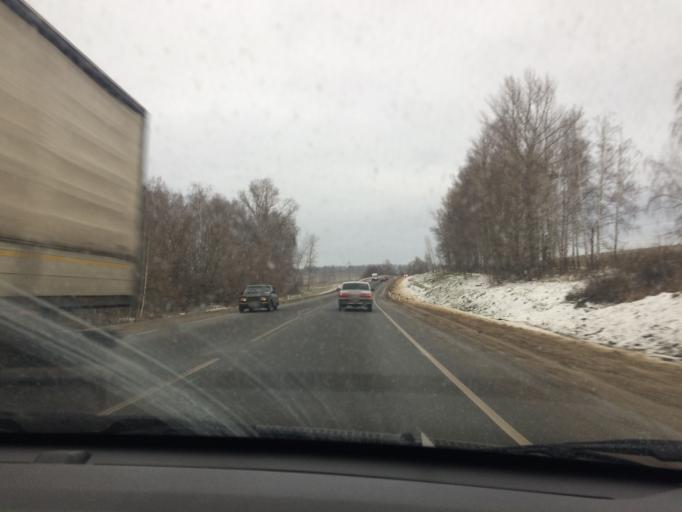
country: RU
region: Tula
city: Gorelki
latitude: 54.2431
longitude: 37.6644
